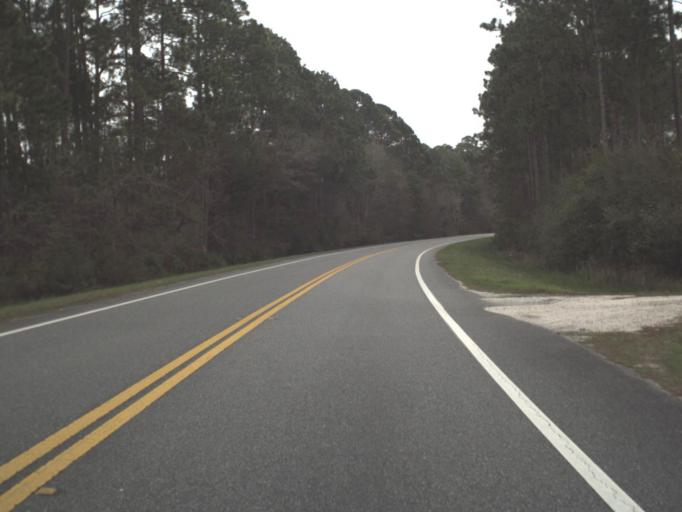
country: US
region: Florida
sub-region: Franklin County
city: Eastpoint
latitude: 29.8273
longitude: -84.8580
